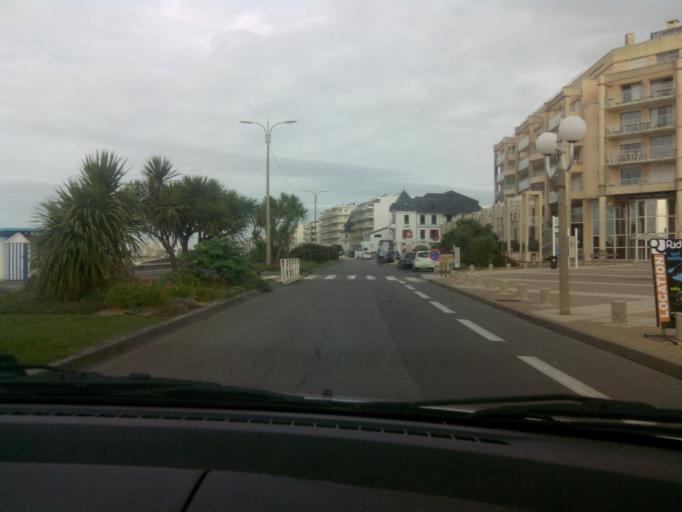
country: FR
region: Pays de la Loire
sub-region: Departement de la Loire-Atlantique
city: Pornichet
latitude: 47.2642
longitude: -2.3443
